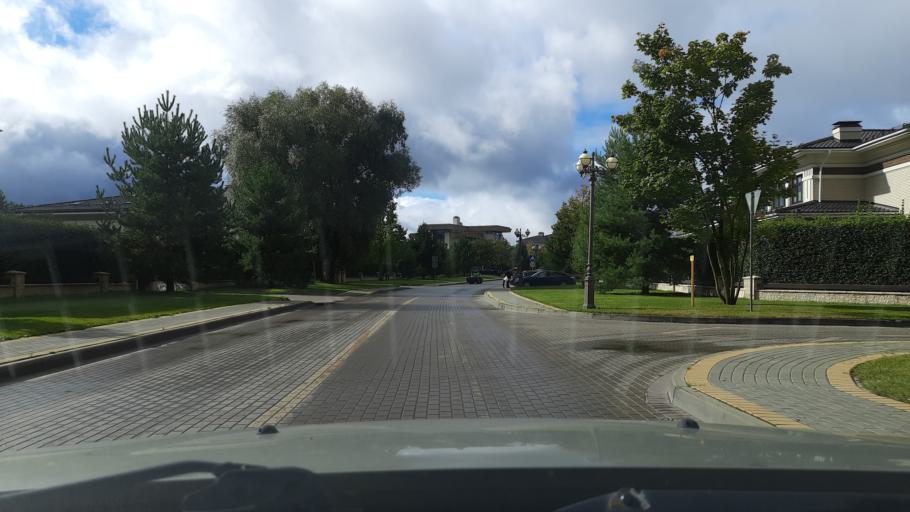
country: RU
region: Moskovskaya
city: Nikolina Gora
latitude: 55.7754
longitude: 37.0518
